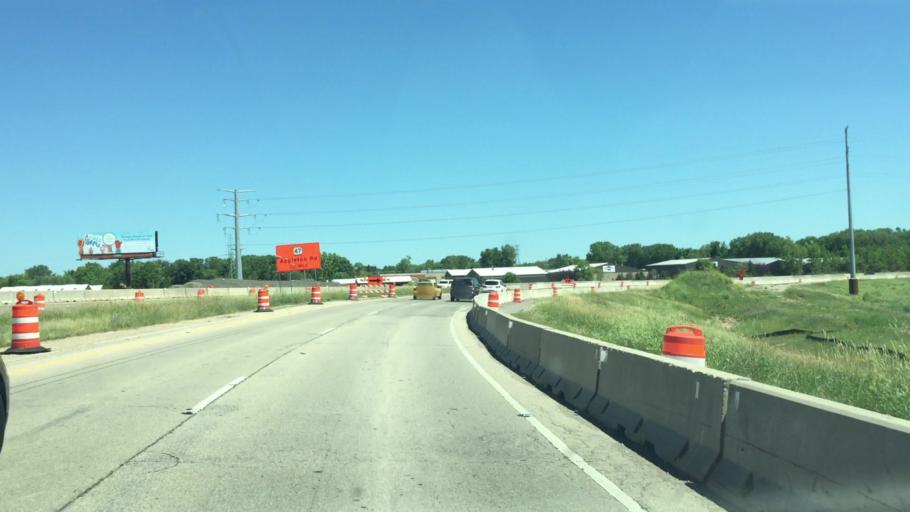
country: US
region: Wisconsin
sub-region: Winnebago County
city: Menasha
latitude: 44.2313
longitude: -88.4407
